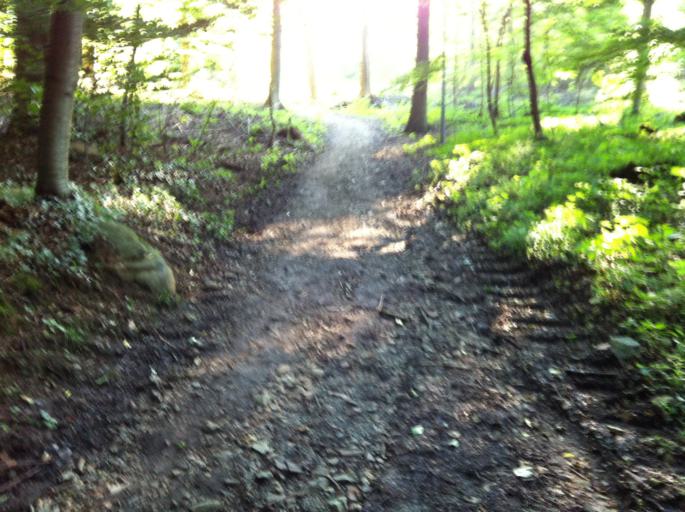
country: DE
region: Baden-Wuerttemberg
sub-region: Karlsruhe Region
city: Heidelberg
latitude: 49.3831
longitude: 8.7093
